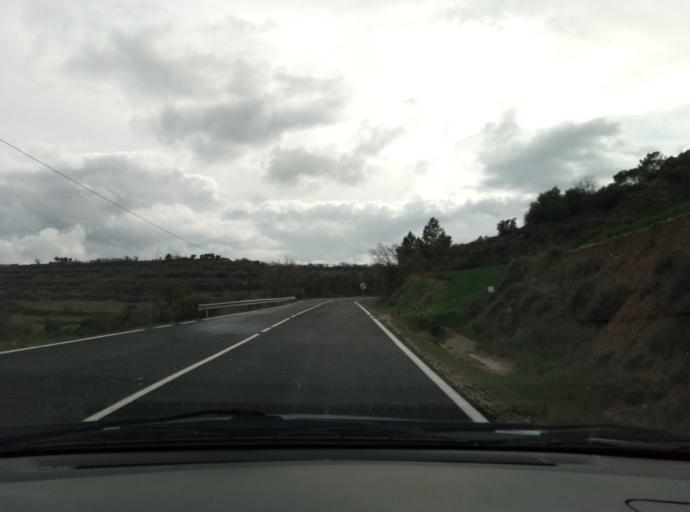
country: ES
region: Catalonia
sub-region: Provincia de Tarragona
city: Santa Coloma de Queralt
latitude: 41.5913
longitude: 1.3405
